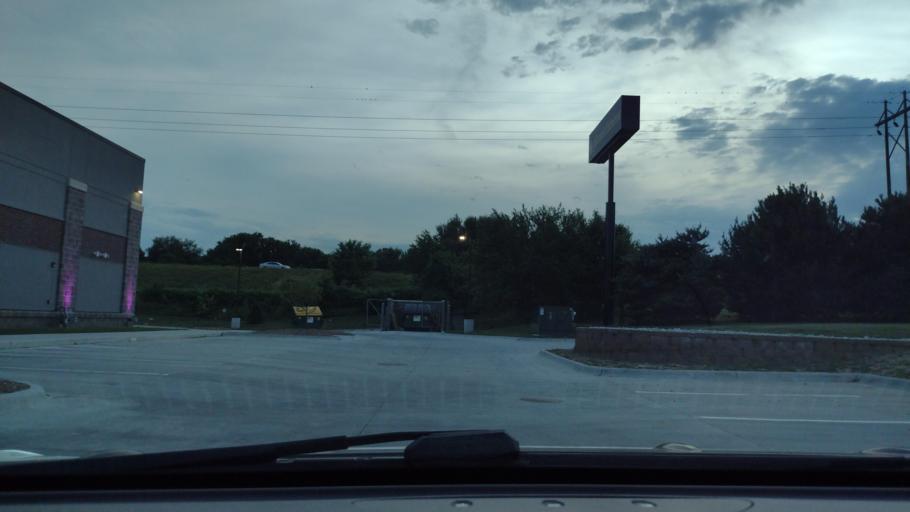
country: US
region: Nebraska
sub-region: Sarpy County
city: Offutt Air Force Base
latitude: 41.1539
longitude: -95.9374
